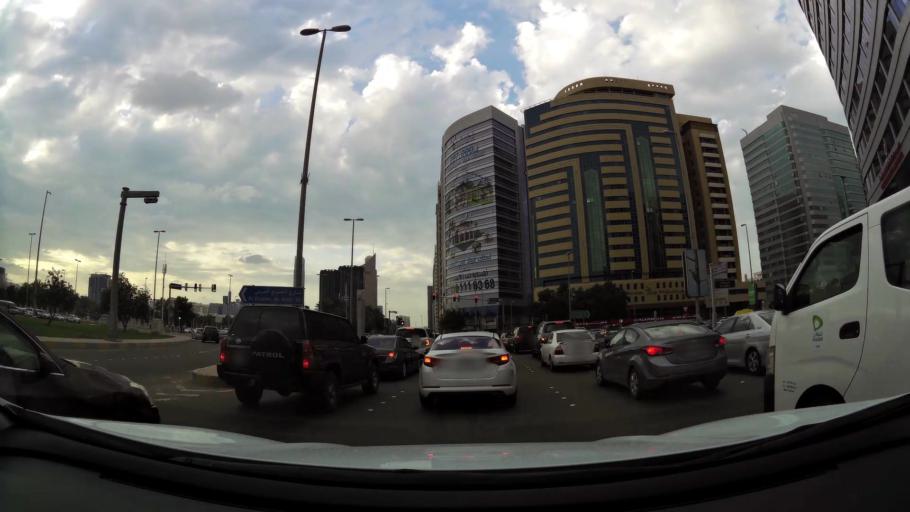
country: AE
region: Abu Dhabi
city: Abu Dhabi
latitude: 24.4755
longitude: 54.3661
